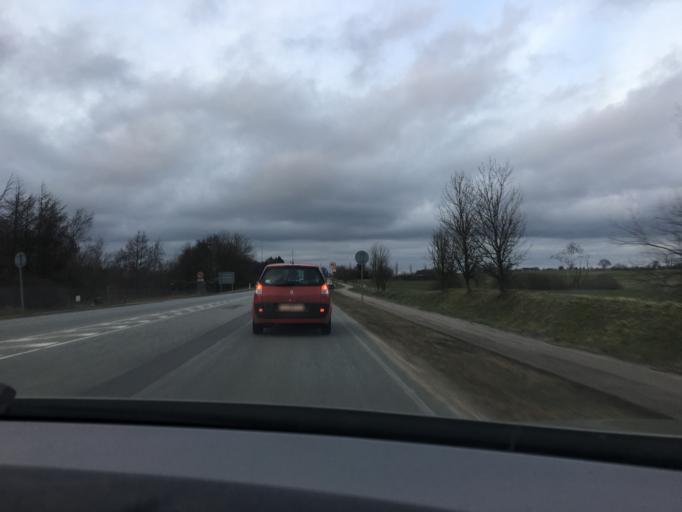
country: DK
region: Central Jutland
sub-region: Hedensted Kommune
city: Hedensted
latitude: 55.7399
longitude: 9.6242
